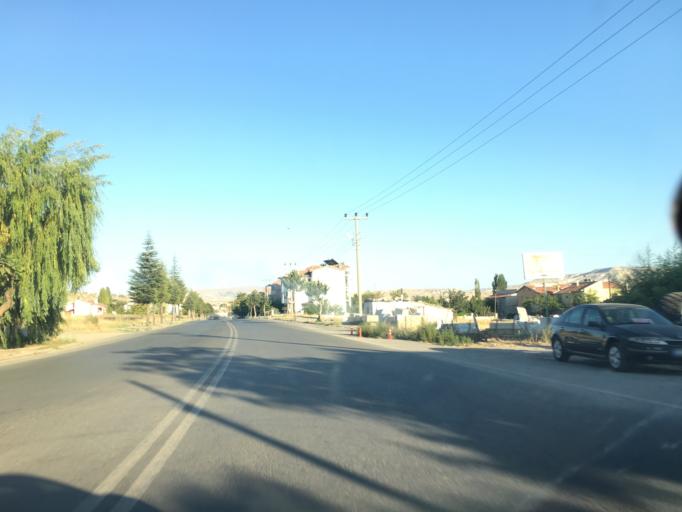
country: TR
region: Nevsehir
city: Avanos
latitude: 38.7205
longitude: 34.8349
